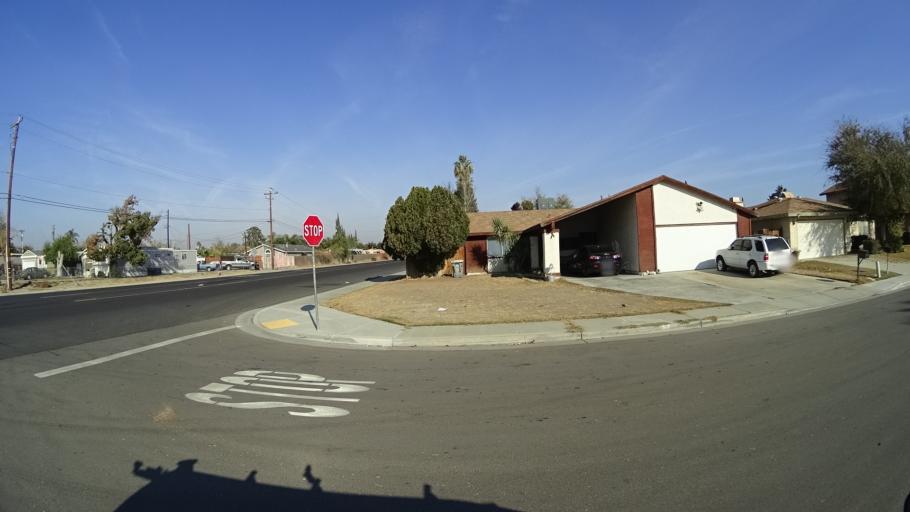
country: US
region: California
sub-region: Kern County
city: Greenfield
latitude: 35.3039
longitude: -119.0299
